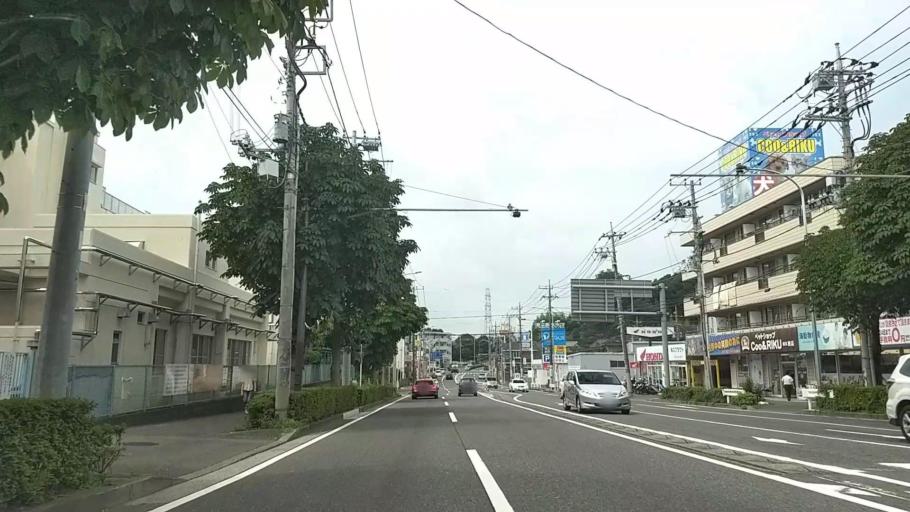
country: JP
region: Kanagawa
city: Minami-rinkan
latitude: 35.4859
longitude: 139.5213
